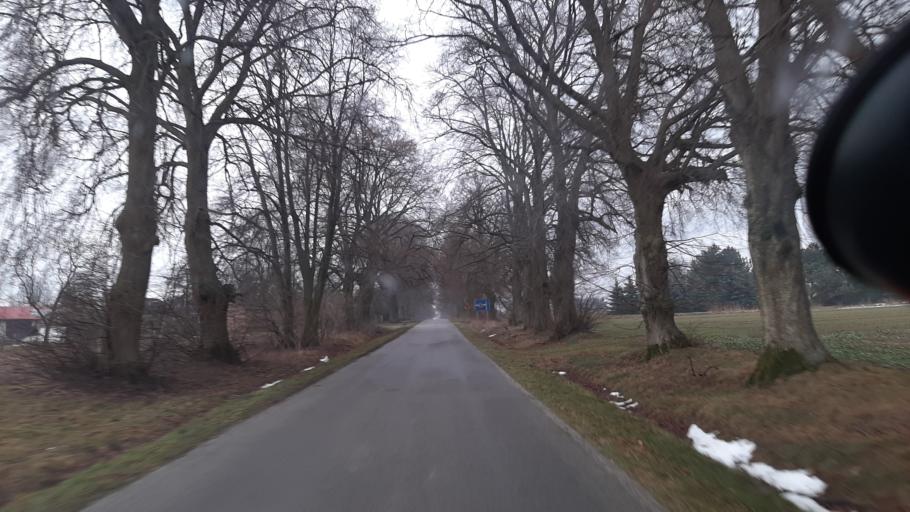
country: PL
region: Lublin Voivodeship
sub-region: Powiat lubelski
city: Lublin
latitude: 51.3418
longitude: 22.5330
